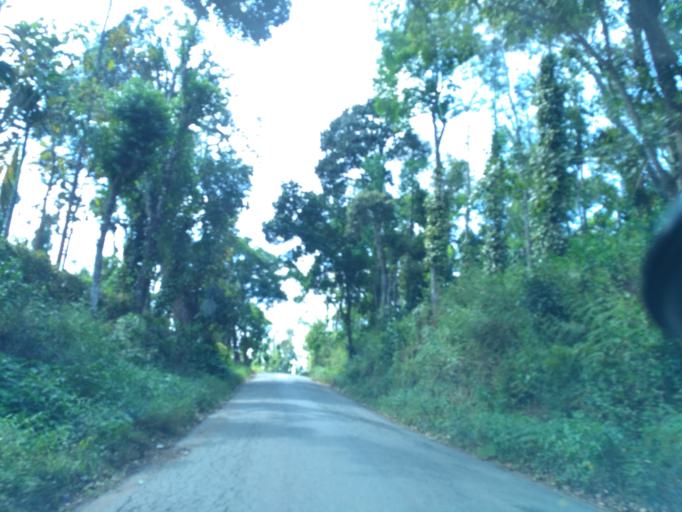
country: IN
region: Karnataka
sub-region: Kodagu
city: Madikeri
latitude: 12.3565
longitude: 75.6432
